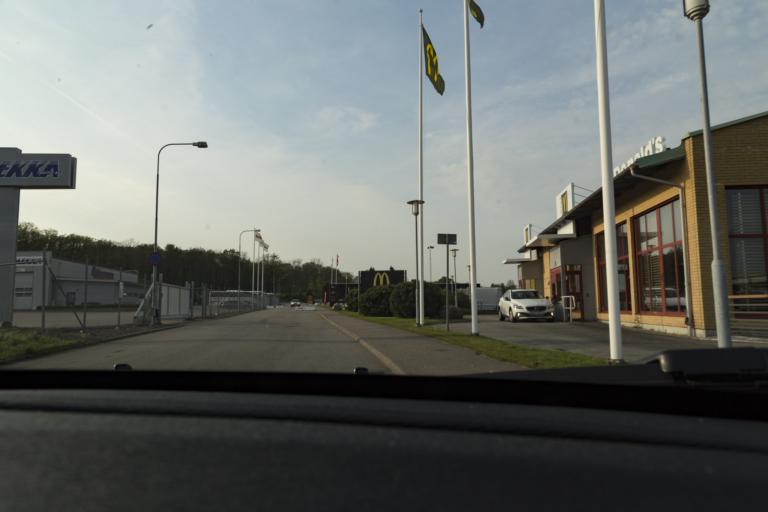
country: SE
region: Halland
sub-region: Varbergs Kommun
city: Varberg
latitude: 57.1687
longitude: 12.2764
